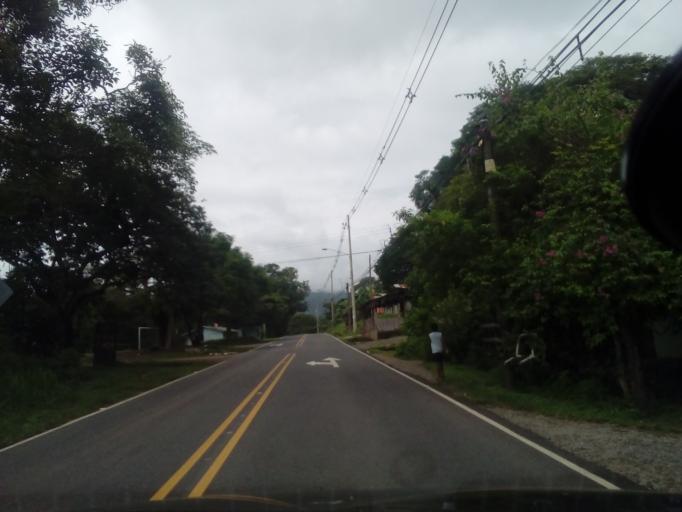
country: CR
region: Guanacaste
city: Samara
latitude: 9.9348
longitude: -85.5165
